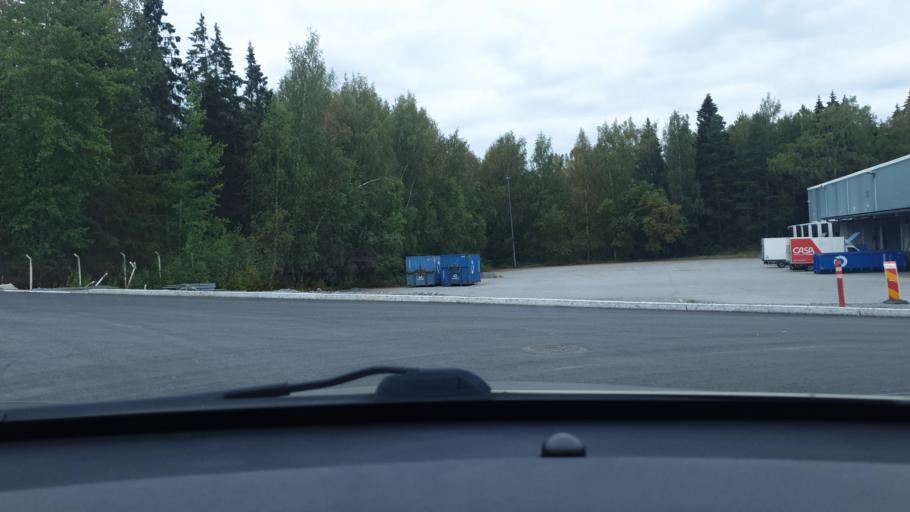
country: FI
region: Ostrobothnia
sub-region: Vaasa
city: Teeriniemi
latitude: 63.0740
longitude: 21.6994
